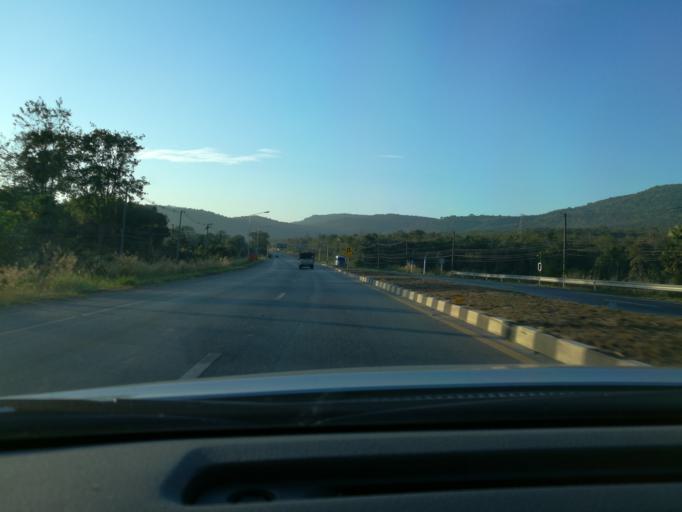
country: TH
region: Phitsanulok
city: Wang Thong
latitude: 16.8636
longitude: 100.5008
